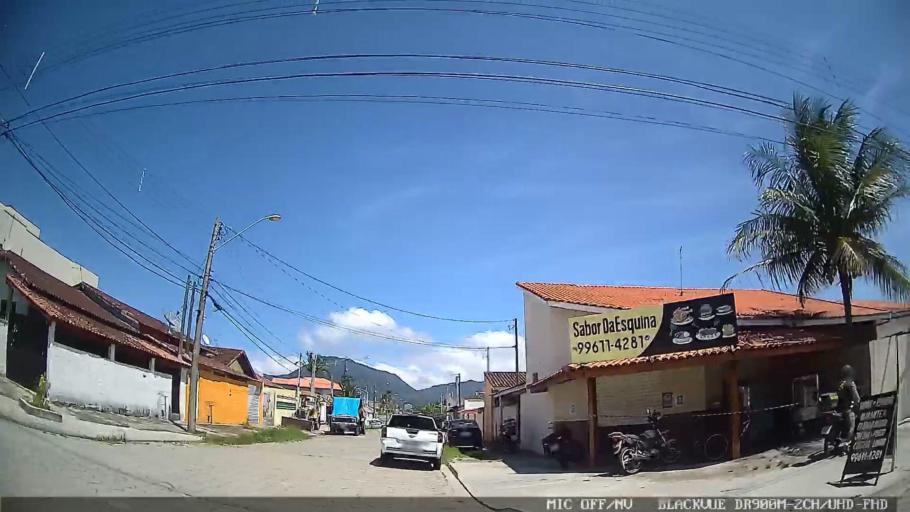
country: BR
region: Sao Paulo
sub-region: Peruibe
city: Peruibe
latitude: -24.3012
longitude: -46.9895
